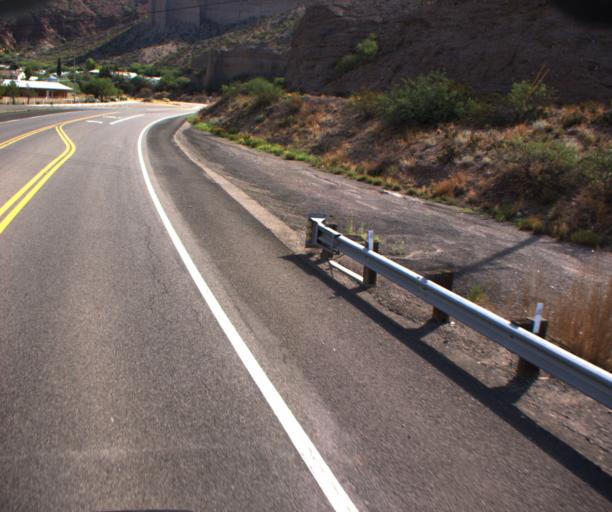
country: US
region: Arizona
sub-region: Greenlee County
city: Clifton
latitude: 33.0412
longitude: -109.2943
